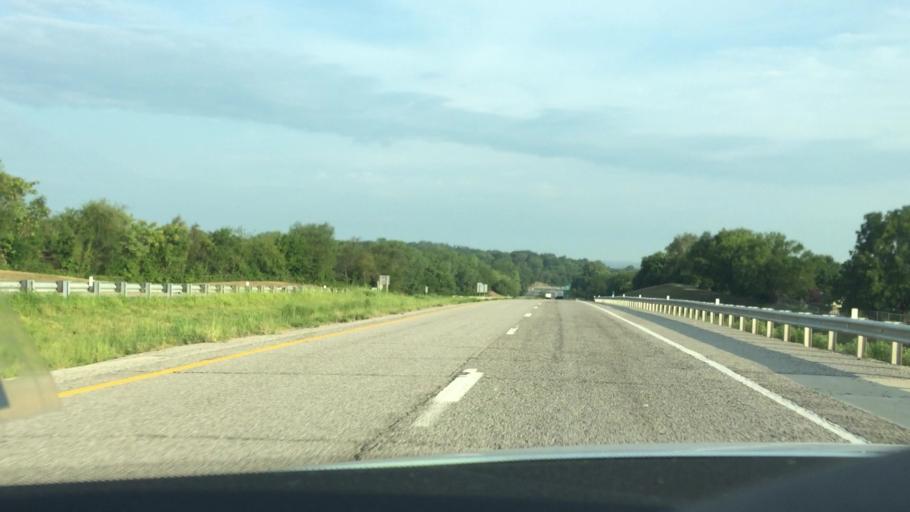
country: US
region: Missouri
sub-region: Buchanan County
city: Saint Joseph
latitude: 39.7222
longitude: -94.8345
